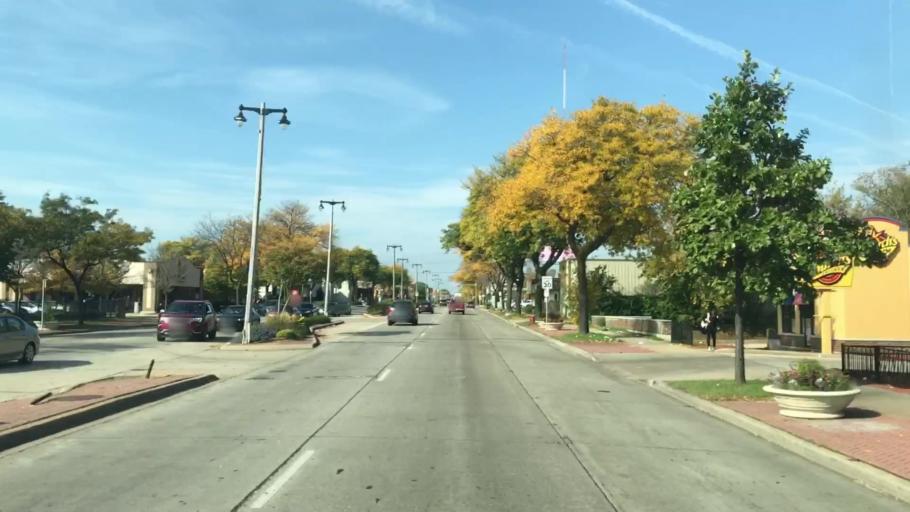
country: US
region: Wisconsin
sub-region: Milwaukee County
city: Shorewood
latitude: 43.0893
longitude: -87.9077
